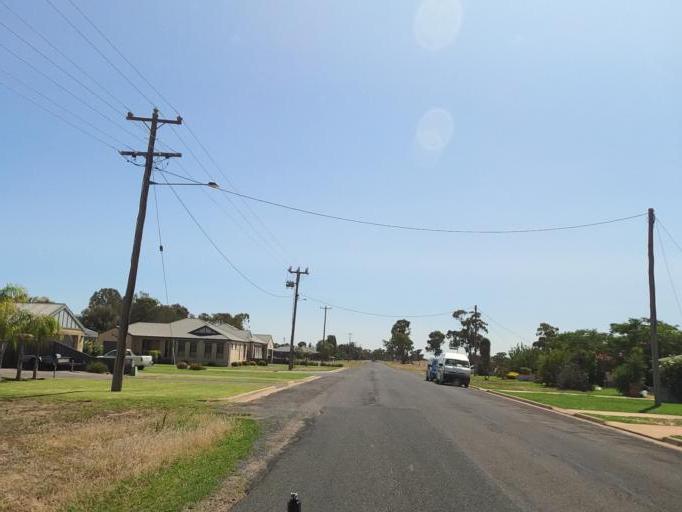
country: AU
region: New South Wales
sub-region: Corowa Shire
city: Mulwala
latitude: -35.9847
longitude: 145.9994
